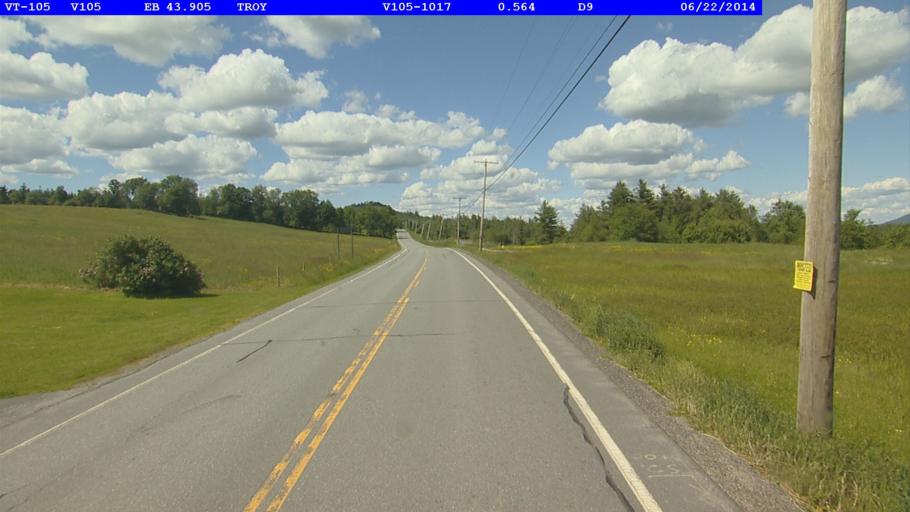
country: US
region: Vermont
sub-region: Orleans County
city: Newport
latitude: 44.9668
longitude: -72.4134
